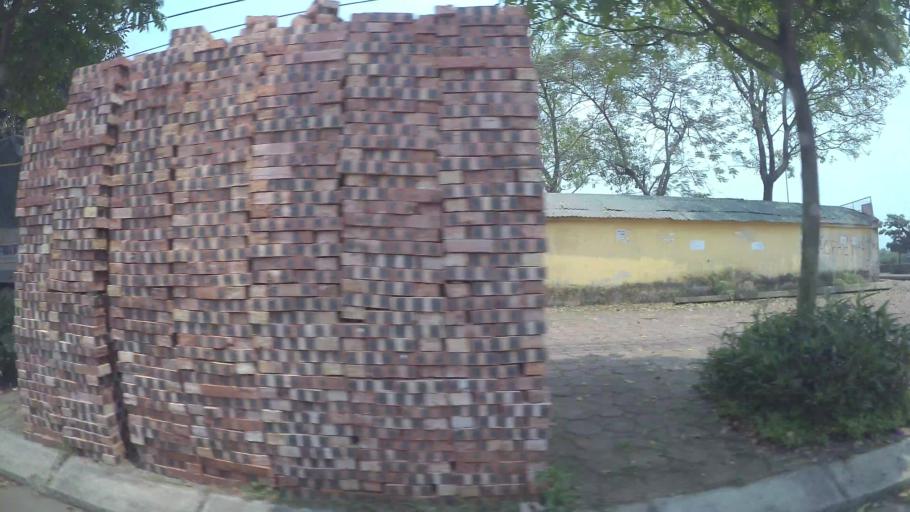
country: VN
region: Ha Noi
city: Van Dien
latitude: 20.9500
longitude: 105.8306
